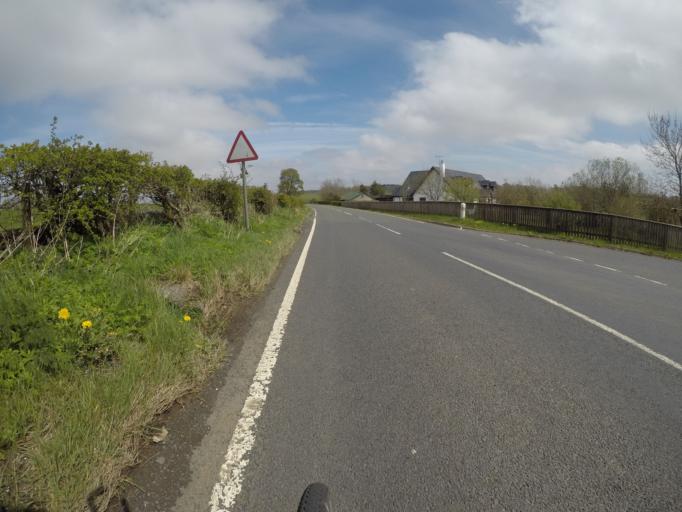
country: GB
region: Scotland
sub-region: East Ayrshire
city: Stewarton
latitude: 55.7053
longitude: -4.4654
